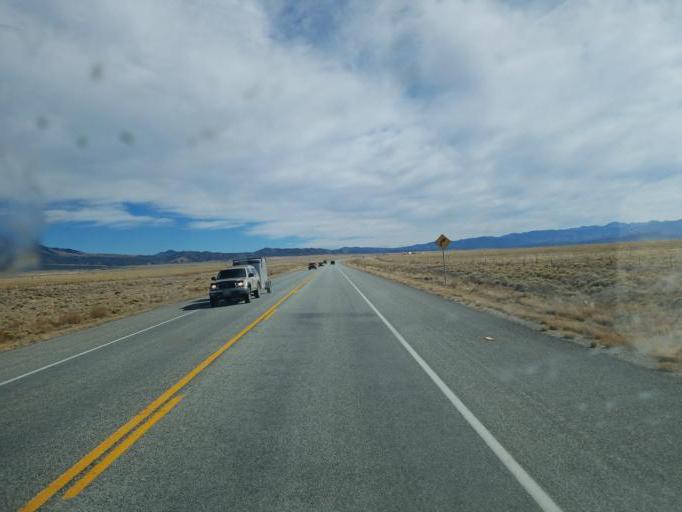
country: US
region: Colorado
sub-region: Alamosa County
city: Alamosa East
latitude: 37.4748
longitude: -105.5936
